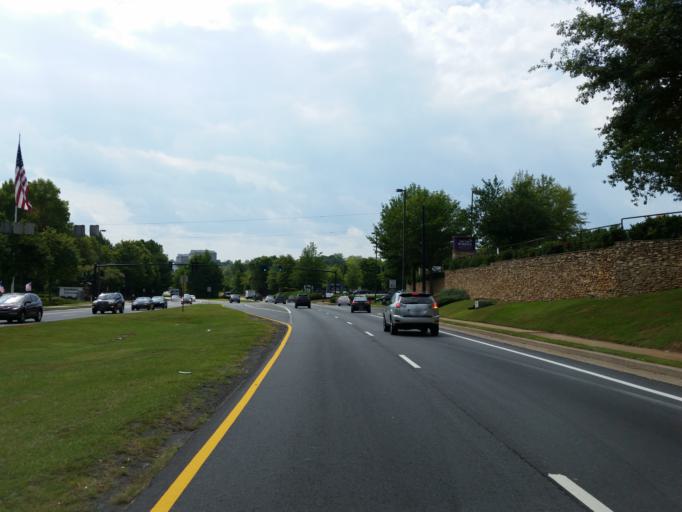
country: US
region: Georgia
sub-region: Fulton County
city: Alpharetta
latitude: 34.0399
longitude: -84.3137
